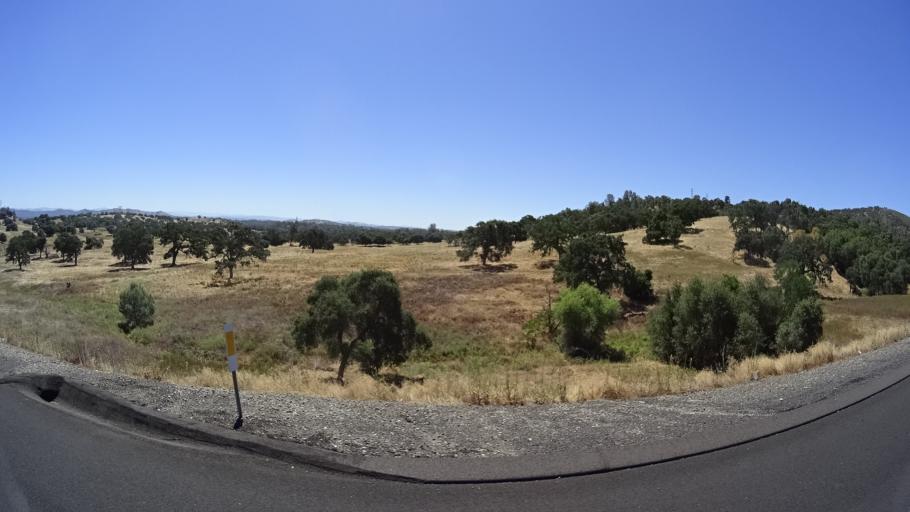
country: US
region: California
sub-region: Calaveras County
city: Copperopolis
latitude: 37.9542
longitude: -120.6939
